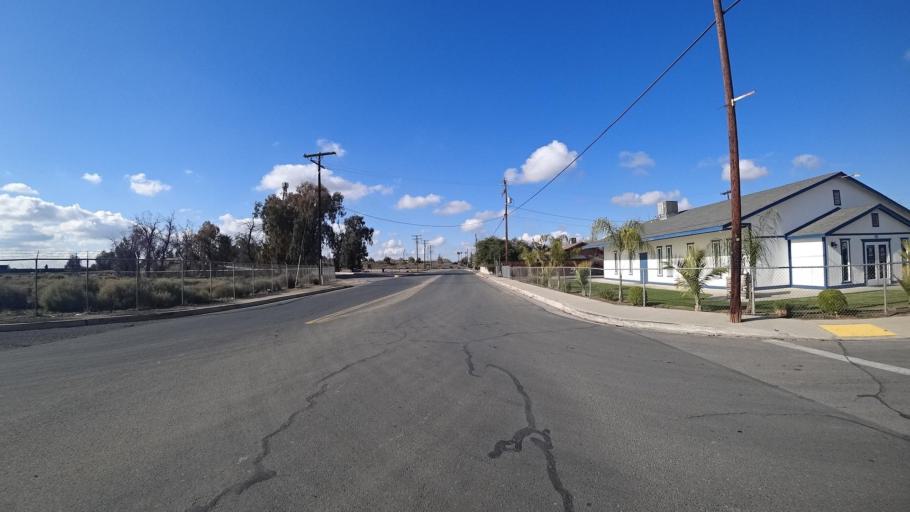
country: US
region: California
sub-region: Kern County
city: McFarland
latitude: 35.6744
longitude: -119.2232
